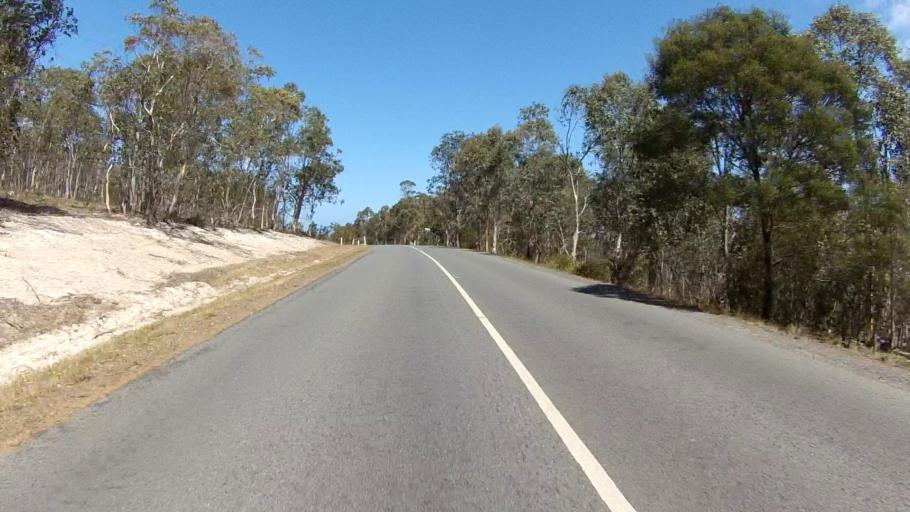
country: AU
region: Tasmania
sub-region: Clarence
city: Sandford
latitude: -42.9746
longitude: 147.4799
